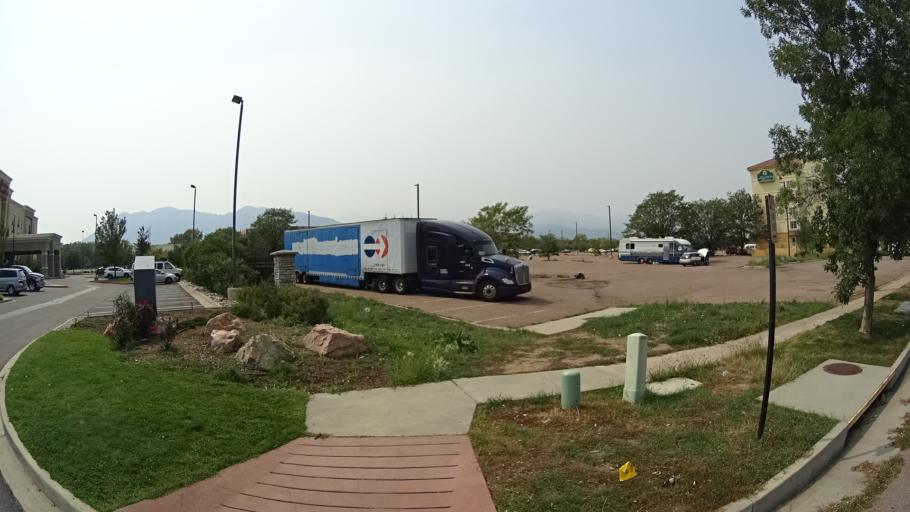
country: US
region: Colorado
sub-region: El Paso County
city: Stratmoor
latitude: 38.7907
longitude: -104.7969
